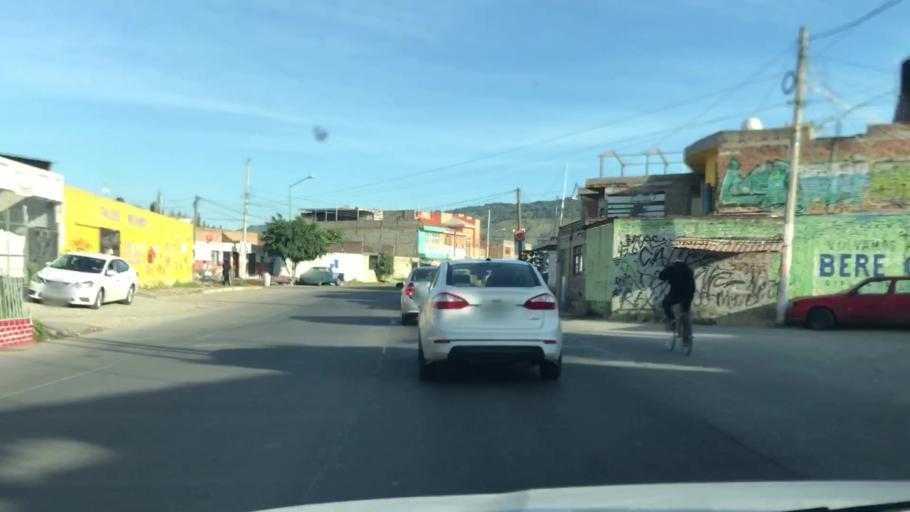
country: MX
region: Jalisco
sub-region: Tlajomulco de Zuniga
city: Palomar
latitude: 20.6325
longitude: -103.4605
